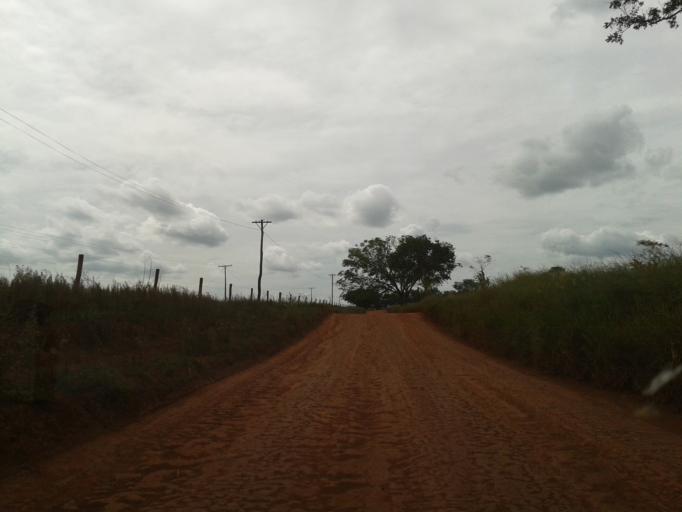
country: BR
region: Minas Gerais
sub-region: Centralina
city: Centralina
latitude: -18.7633
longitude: -49.2211
